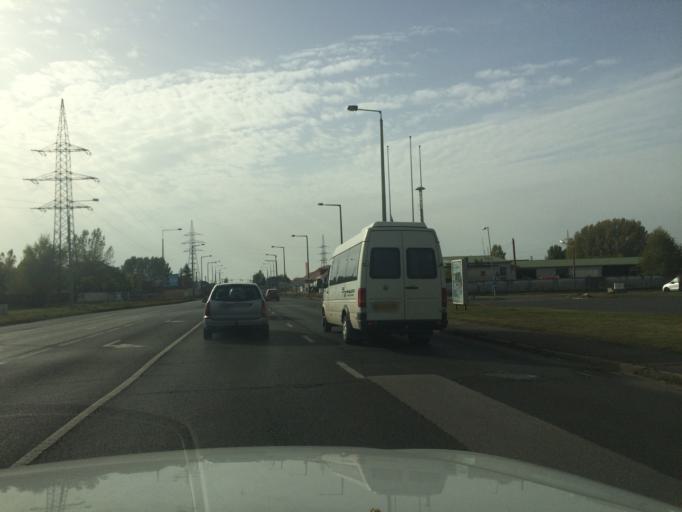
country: HU
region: Szabolcs-Szatmar-Bereg
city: Nyiregyhaza
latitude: 47.9362
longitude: 21.7188
